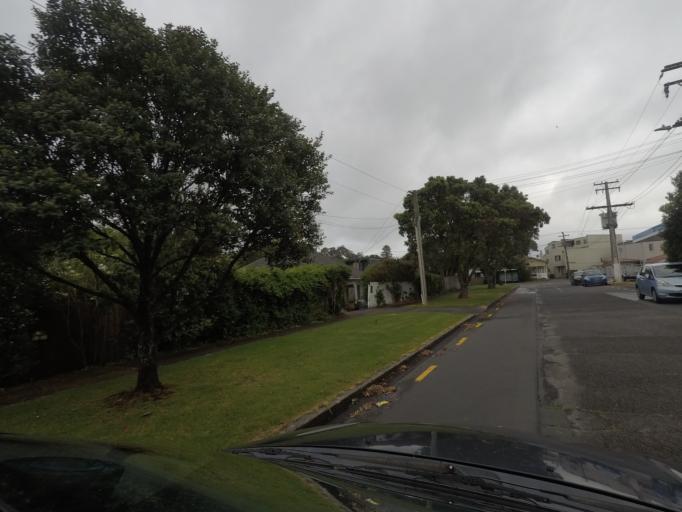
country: NZ
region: Auckland
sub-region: Auckland
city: Auckland
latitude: -36.8946
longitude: 174.7267
